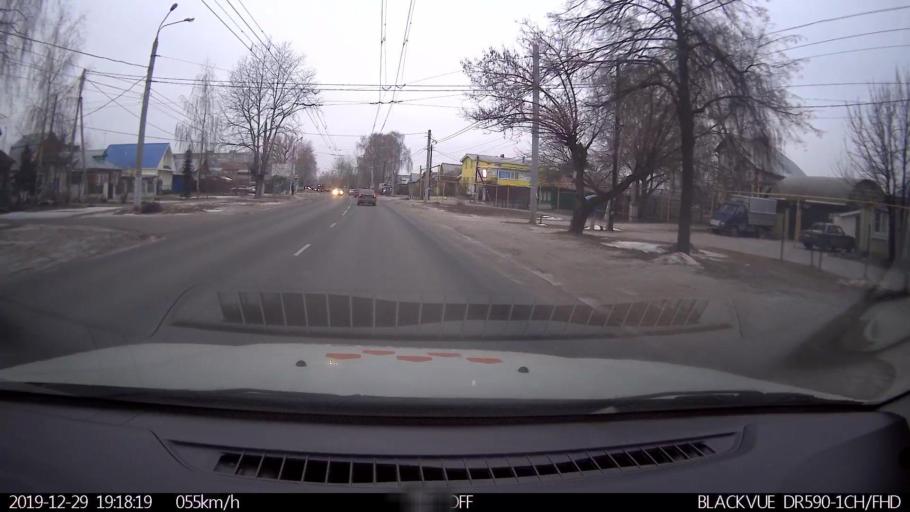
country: RU
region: Nizjnij Novgorod
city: Gorbatovka
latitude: 56.3813
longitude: 43.8050
